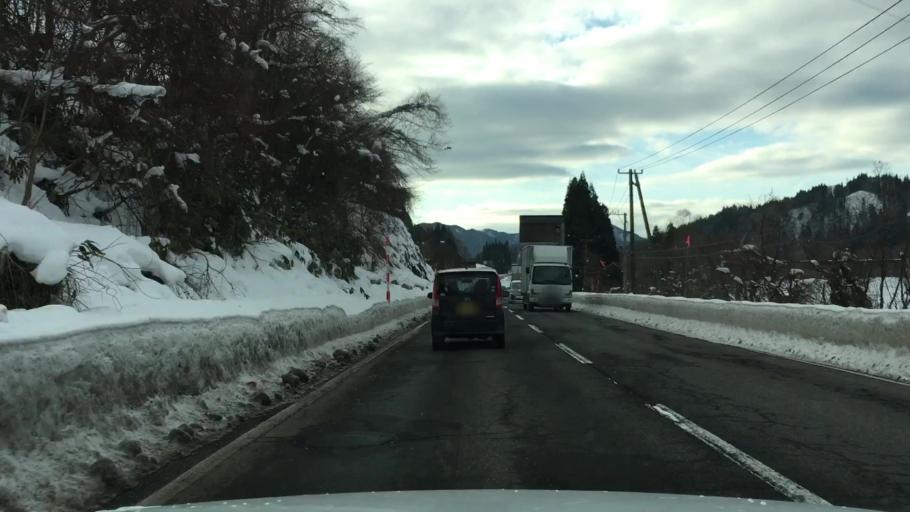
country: JP
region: Aomori
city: Kuroishi
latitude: 40.4604
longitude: 140.6359
